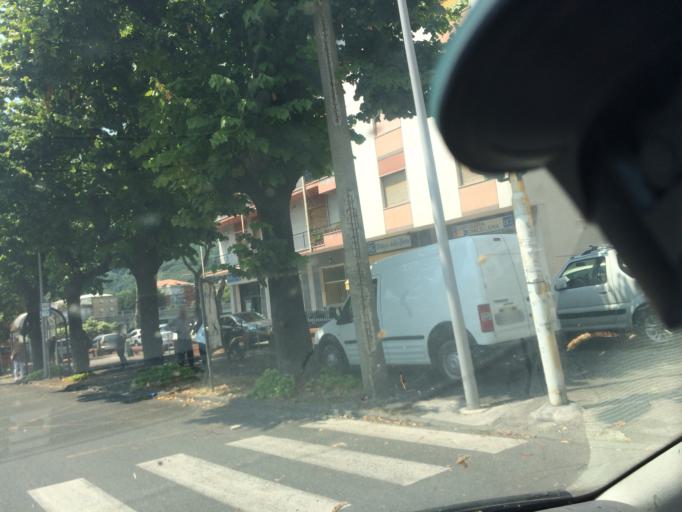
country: IT
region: Tuscany
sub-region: Provincia di Massa-Carrara
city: Carrara
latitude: 44.0706
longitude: 10.0876
